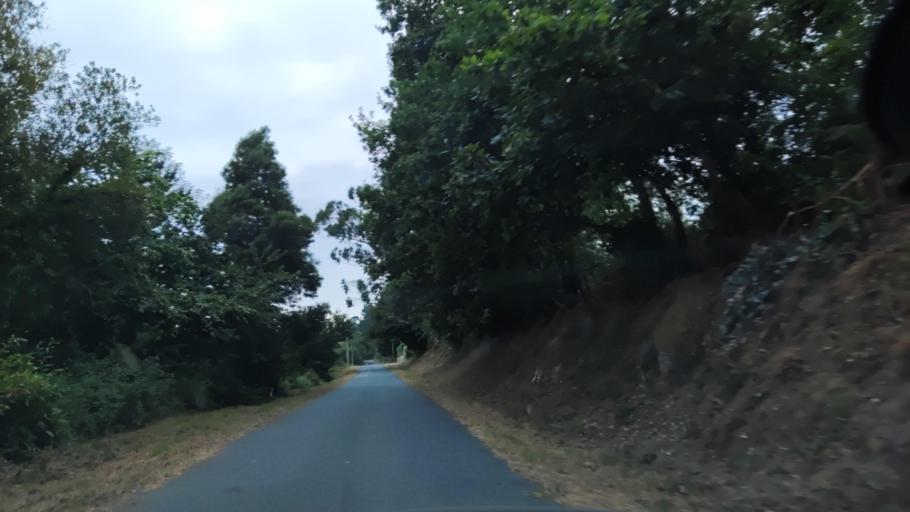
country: ES
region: Galicia
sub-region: Provincia de Pontevedra
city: Catoira
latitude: 42.7064
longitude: -8.7228
